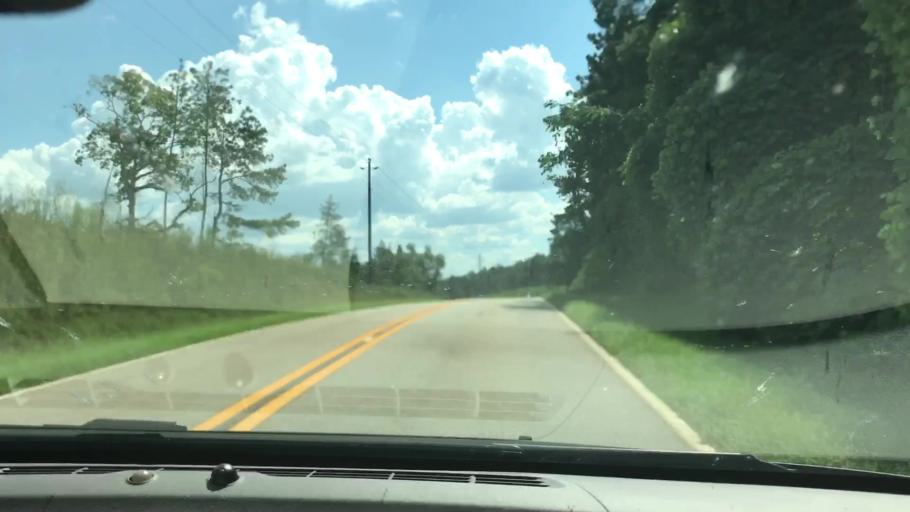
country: US
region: Georgia
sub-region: Troup County
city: La Grange
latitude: 33.1369
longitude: -85.1167
